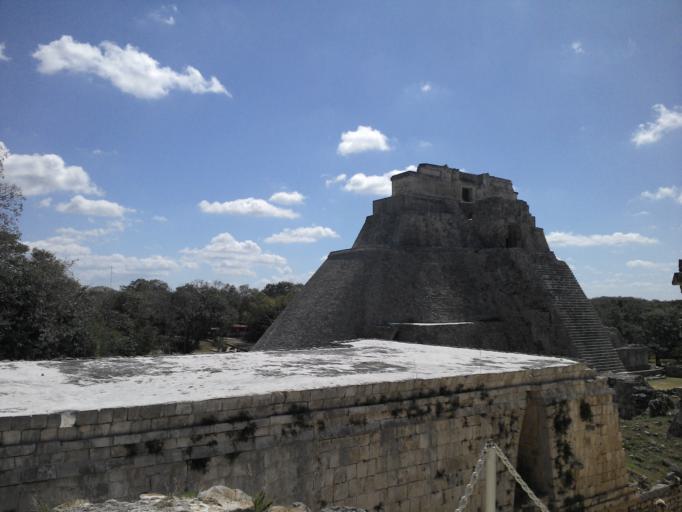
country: MX
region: Yucatan
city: Santa Elena
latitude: 20.3615
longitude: -89.7702
